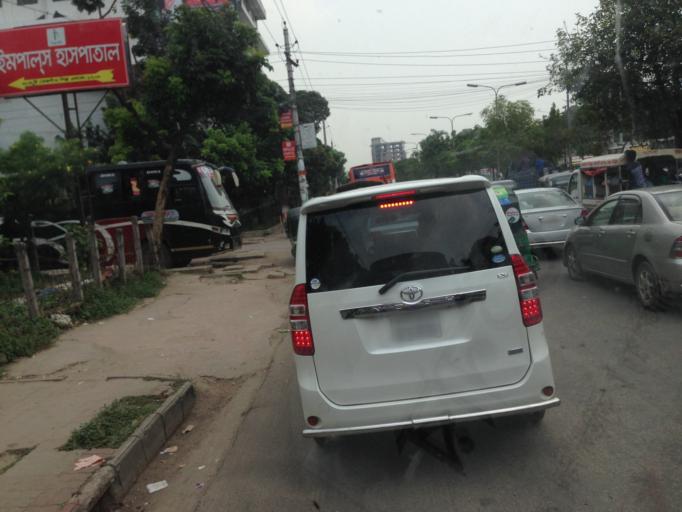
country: BD
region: Dhaka
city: Paltan
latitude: 23.7672
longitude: 90.4005
